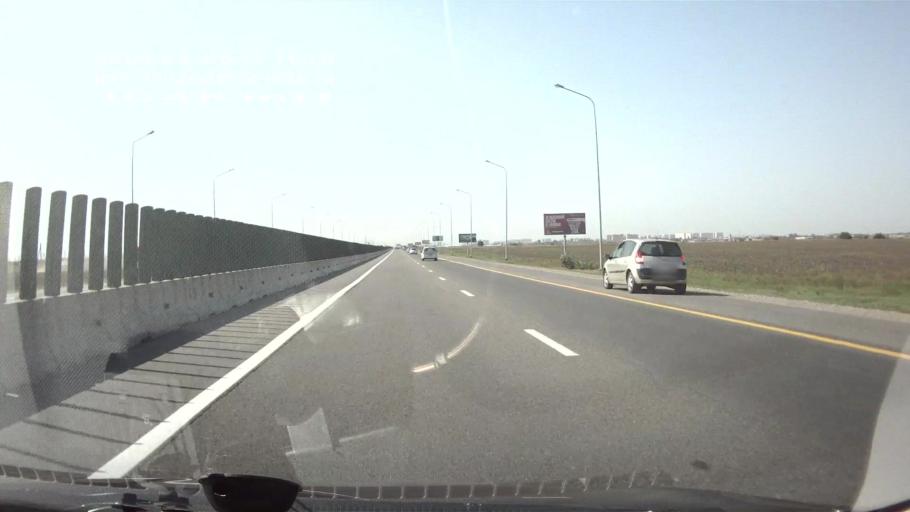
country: RU
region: Krasnodarskiy
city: Pashkovskiy
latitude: 45.0196
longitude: 39.1868
